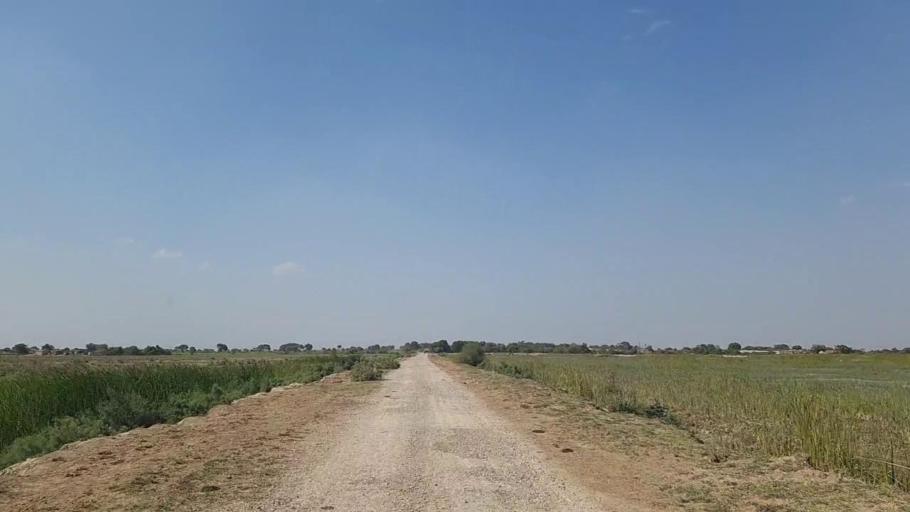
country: PK
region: Sindh
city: Jati
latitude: 24.5150
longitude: 68.2945
